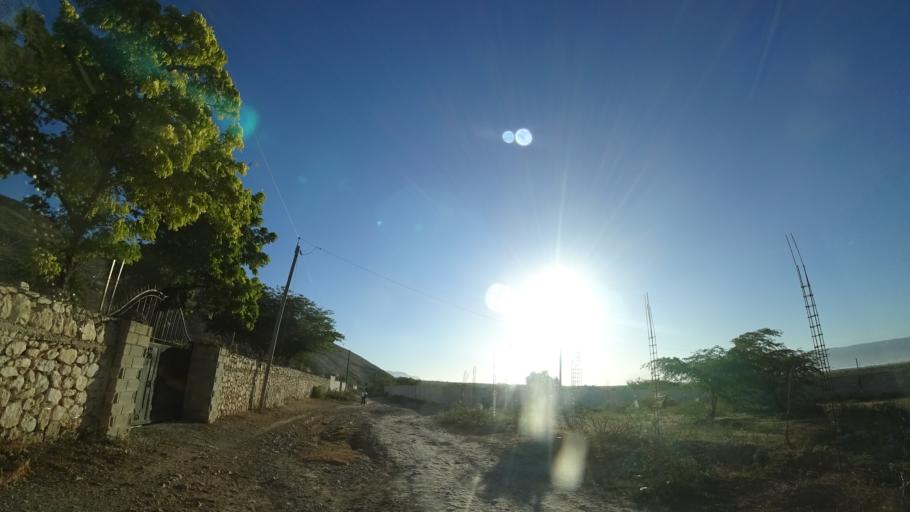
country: HT
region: Ouest
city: Croix des Bouquets
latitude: 18.6626
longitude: -72.2234
